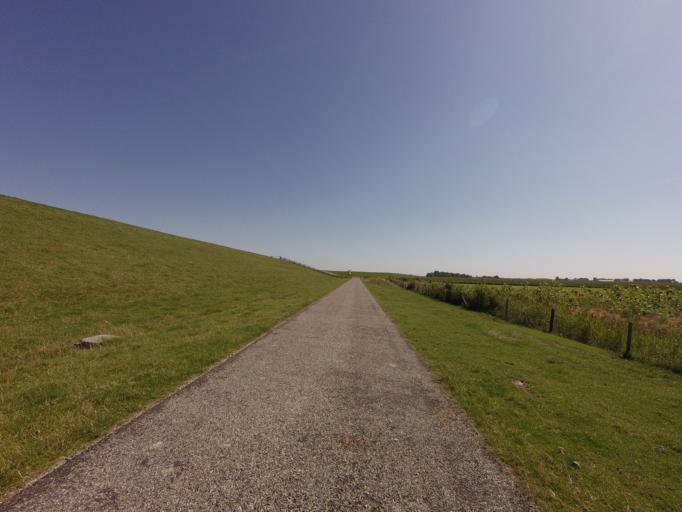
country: NL
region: Friesland
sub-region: Gemeente Dongeradeel
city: Anjum
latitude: 53.4007
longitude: 6.0961
